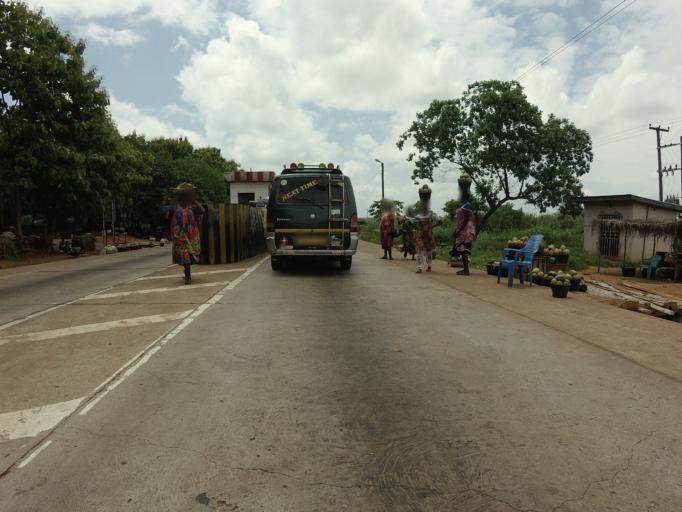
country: GH
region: Brong-Ahafo
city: Techiman
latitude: 7.6522
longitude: -1.8767
